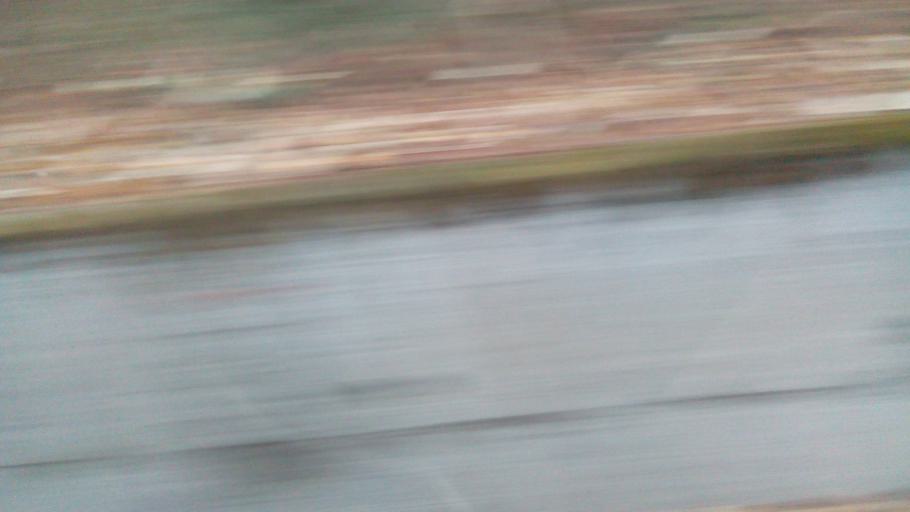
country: TW
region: Taiwan
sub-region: Hualien
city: Hualian
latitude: 24.3241
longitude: 121.3030
